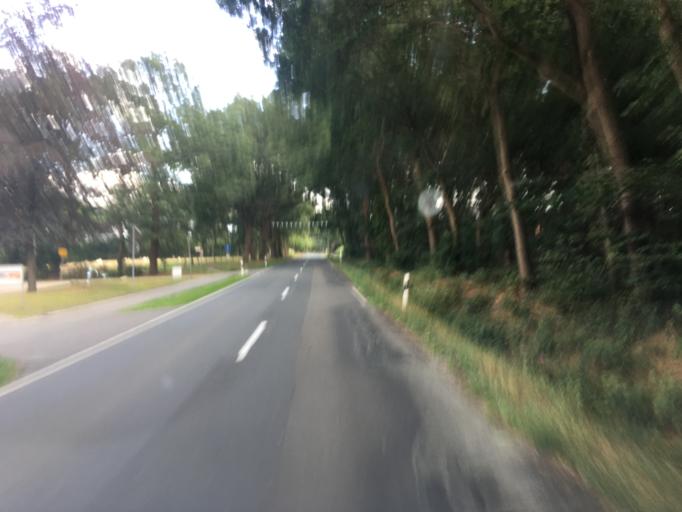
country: DE
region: Lower Saxony
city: Friesoythe
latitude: 53.0786
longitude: 7.8399
